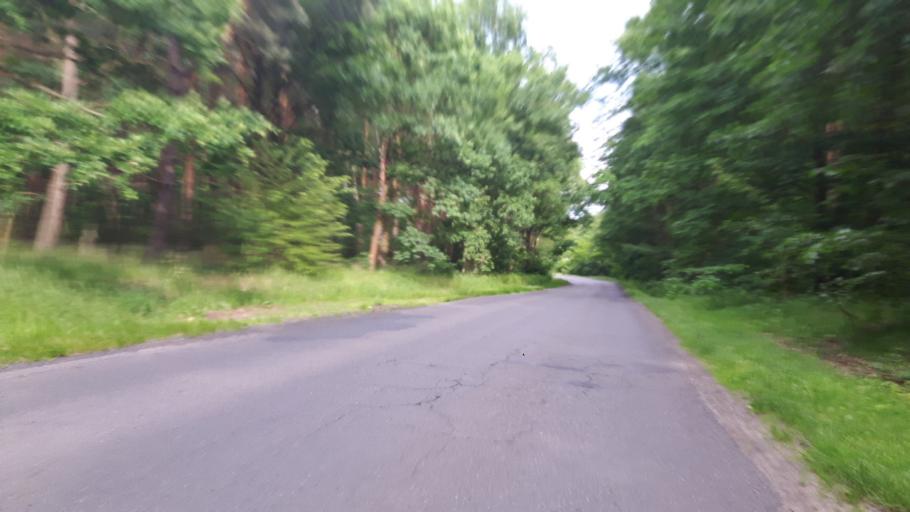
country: PL
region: West Pomeranian Voivodeship
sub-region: Powiat goleniowski
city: Goleniow
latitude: 53.4525
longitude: 14.7502
